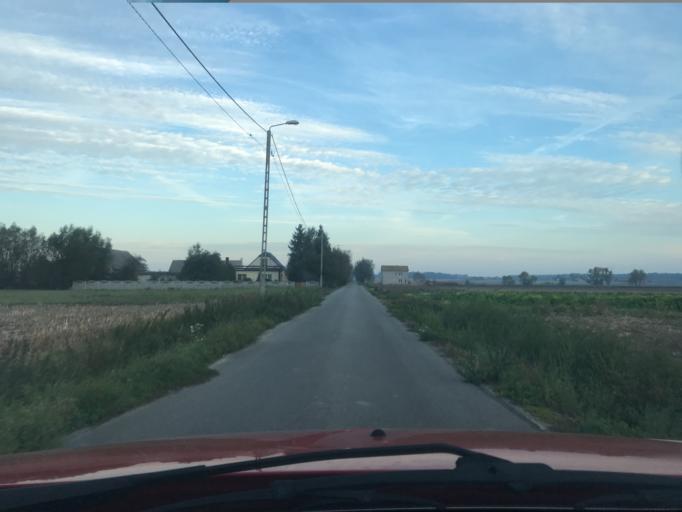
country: PL
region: Greater Poland Voivodeship
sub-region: Powiat ostrowski
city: Skalmierzyce
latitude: 51.7618
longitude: 17.8984
